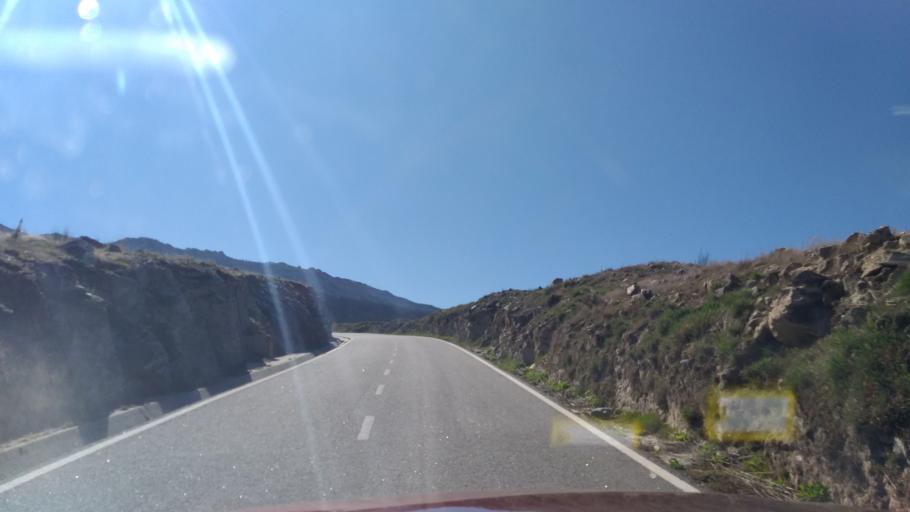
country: PT
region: Guarda
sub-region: Manteigas
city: Manteigas
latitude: 40.4979
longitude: -7.5215
